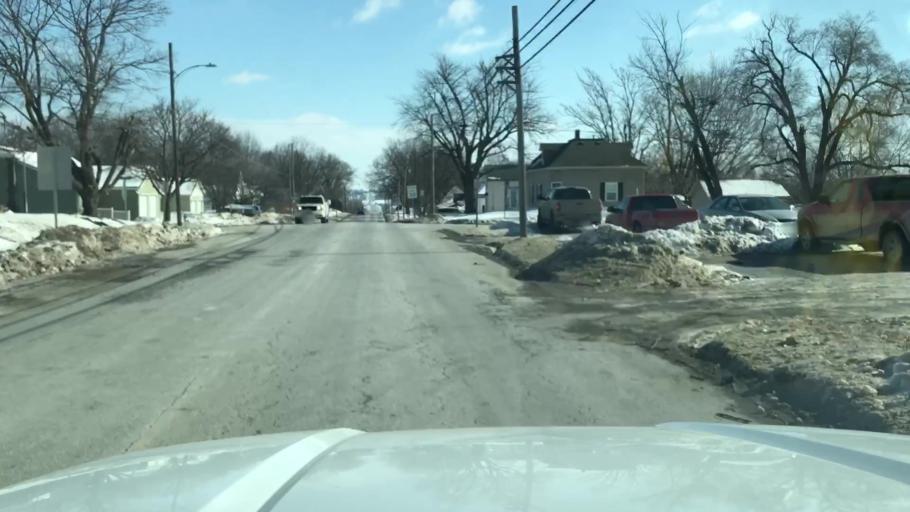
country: US
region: Missouri
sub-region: Nodaway County
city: Maryville
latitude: 40.3455
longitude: -94.8664
